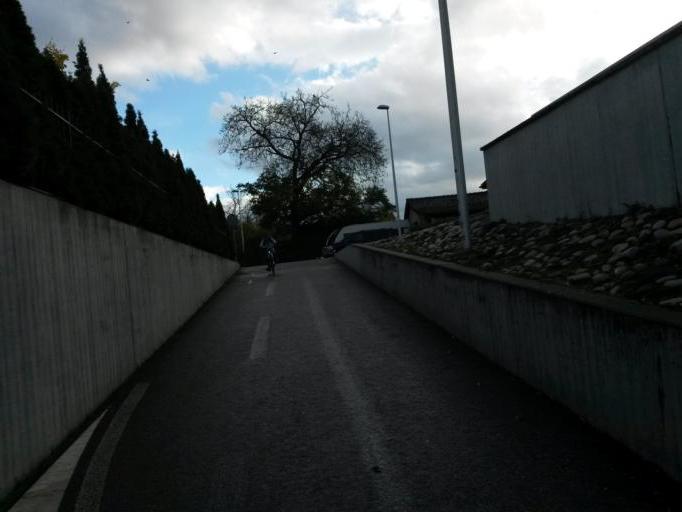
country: CH
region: Solothurn
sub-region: Bezirk Wasseramt
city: Derendingen
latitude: 47.2018
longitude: 7.5866
